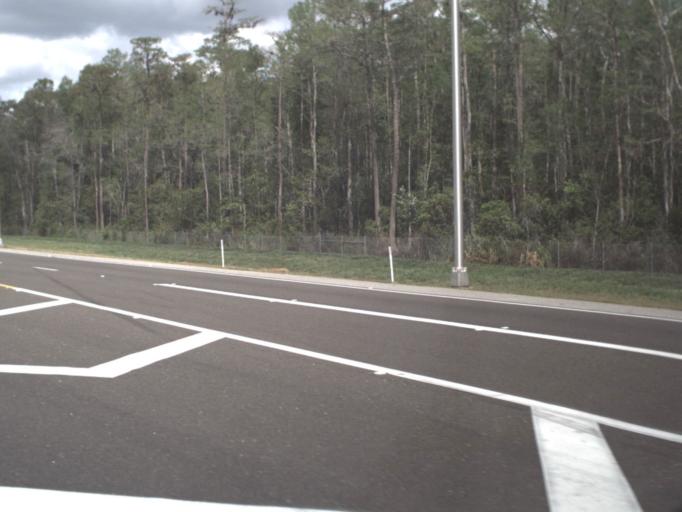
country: US
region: Florida
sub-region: Orange County
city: Wedgefield
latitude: 28.4522
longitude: -81.0536
